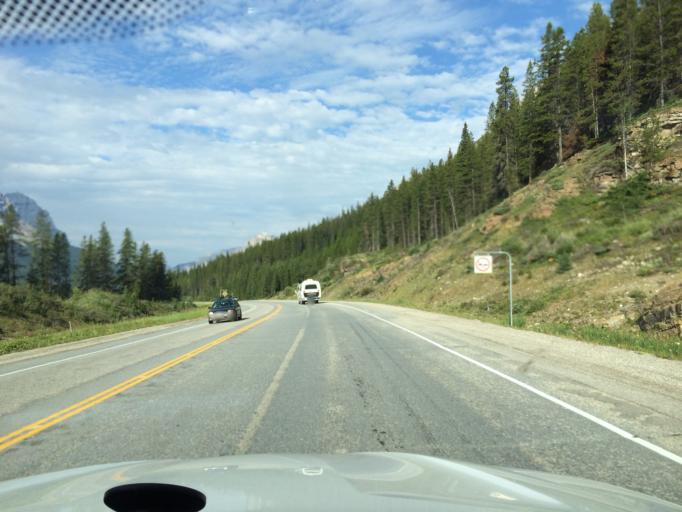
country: CA
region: Alberta
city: Lake Louise
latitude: 51.4522
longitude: -116.3071
